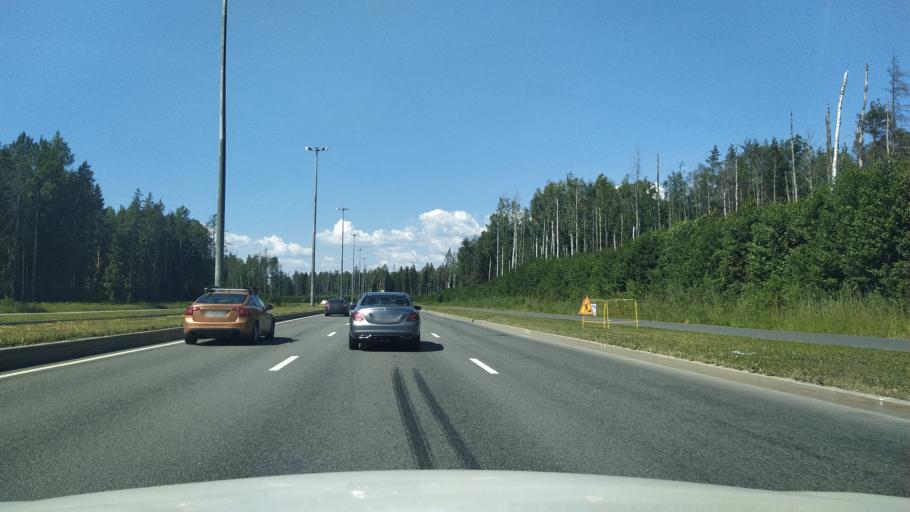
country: RU
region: St.-Petersburg
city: Levashovo
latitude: 60.0603
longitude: 30.2183
